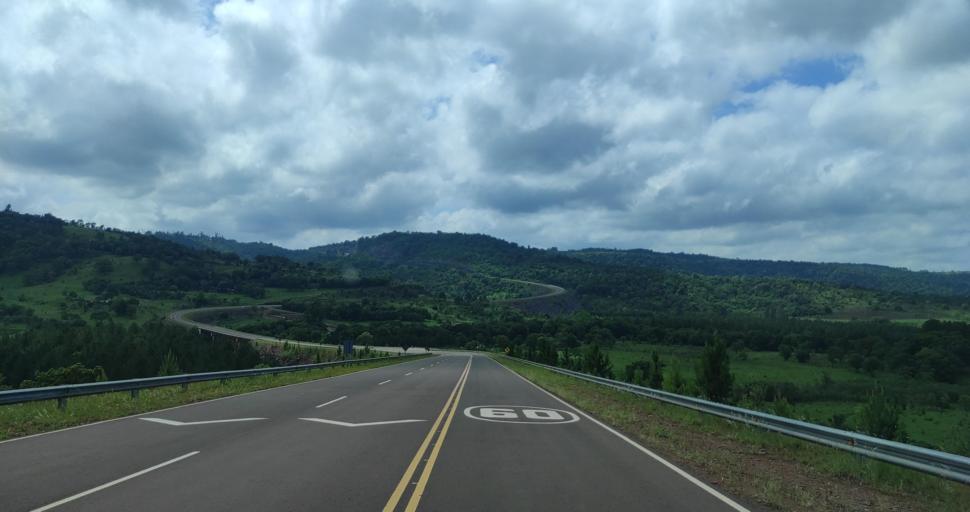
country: AR
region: Misiones
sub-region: Departamento de Veinticinco de Mayo
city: Veinticinco de Mayo
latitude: -27.3773
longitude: -54.8281
